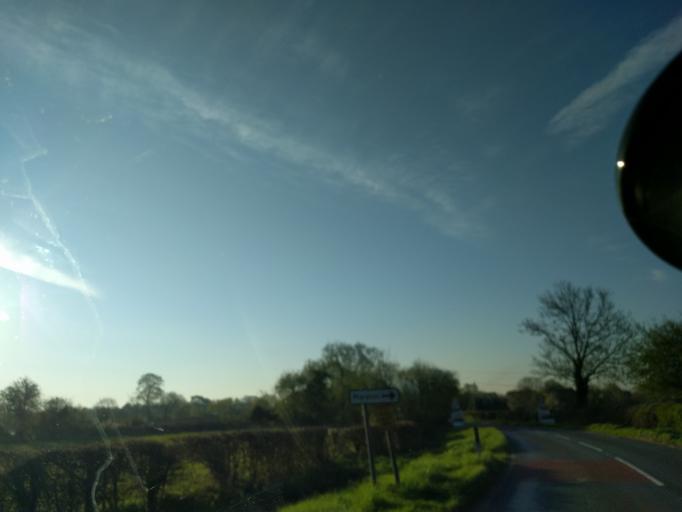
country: GB
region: England
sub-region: Wiltshire
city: Worton
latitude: 51.3179
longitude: -2.0474
